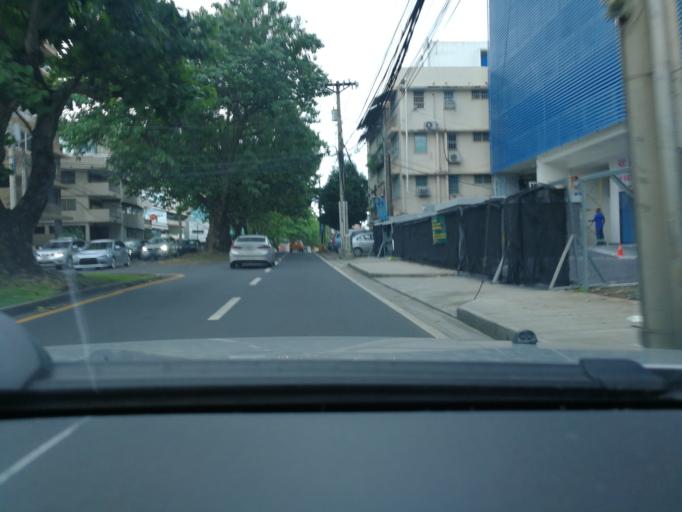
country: PA
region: Panama
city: Panama
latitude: 8.9937
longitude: -79.5244
